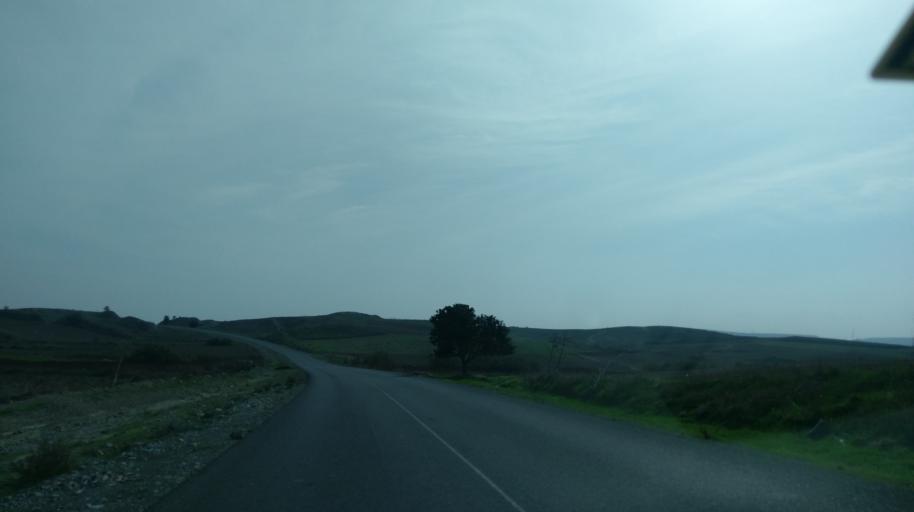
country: CY
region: Keryneia
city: Lapithos
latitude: 35.2823
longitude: 33.0961
